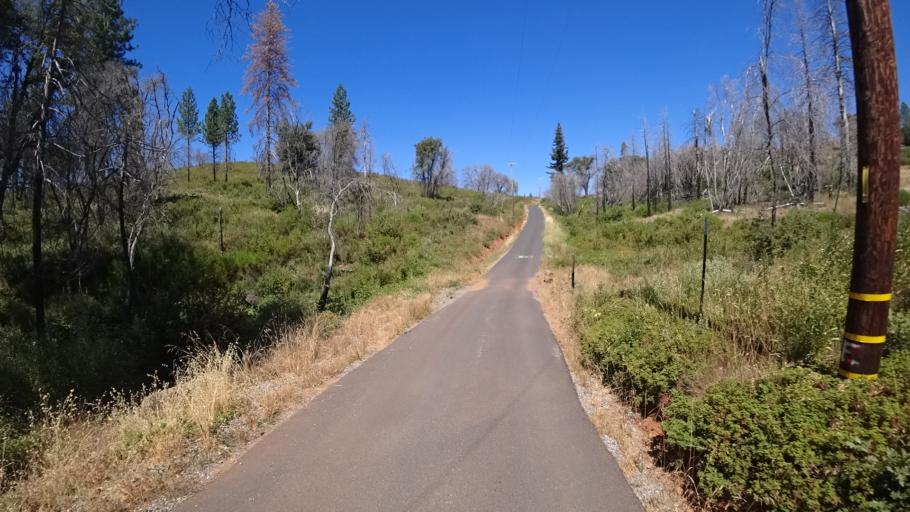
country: US
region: California
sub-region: Calaveras County
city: Mountain Ranch
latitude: 38.2738
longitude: -120.5596
